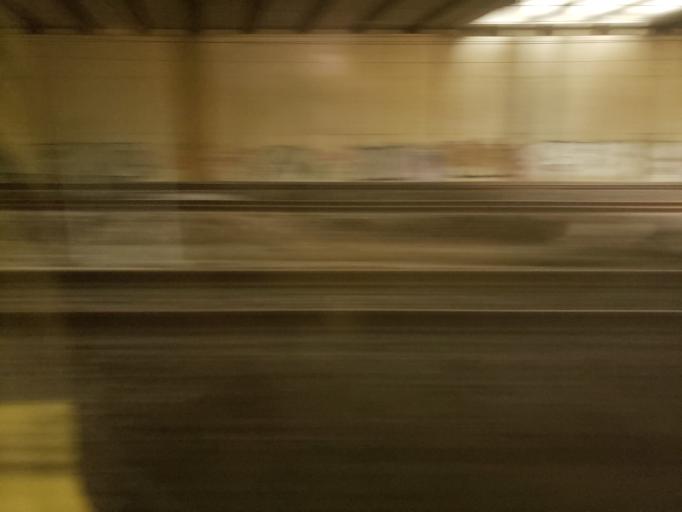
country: FR
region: Ile-de-France
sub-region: Departement de Seine-et-Marne
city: Serris
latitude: 48.8547
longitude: 2.7799
